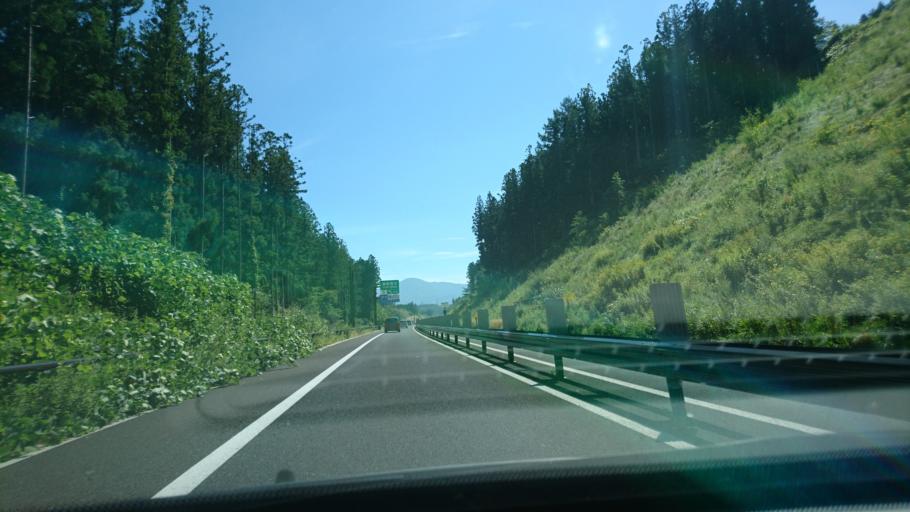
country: JP
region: Iwate
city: Tono
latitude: 39.3251
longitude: 141.4962
